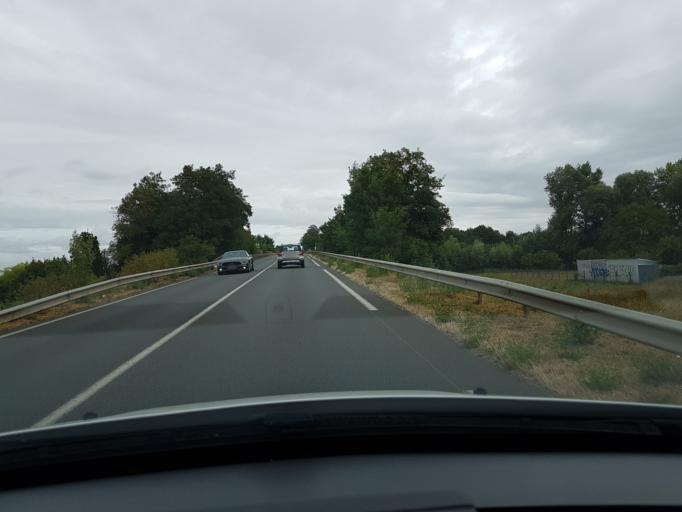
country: FR
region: Centre
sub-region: Departement d'Indre-et-Loire
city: La Ville-aux-Dames
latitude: 47.3874
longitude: 0.7862
